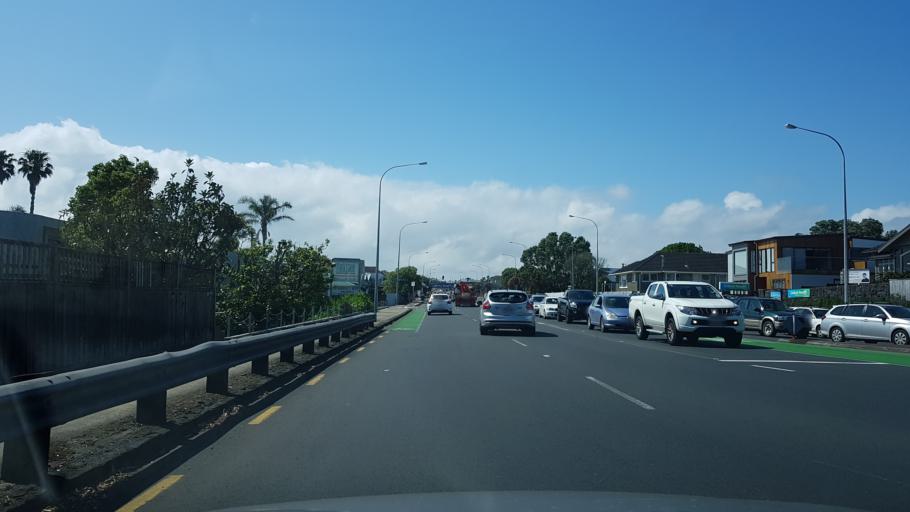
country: NZ
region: Auckland
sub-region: Auckland
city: North Shore
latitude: -36.7933
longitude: 174.7757
